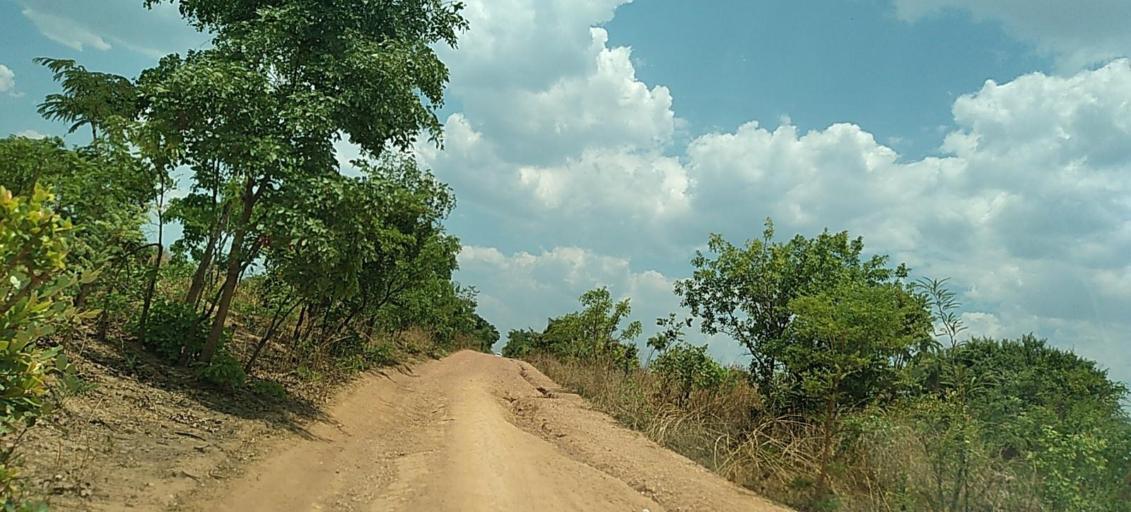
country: ZM
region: Copperbelt
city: Luanshya
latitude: -13.3749
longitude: 28.4259
